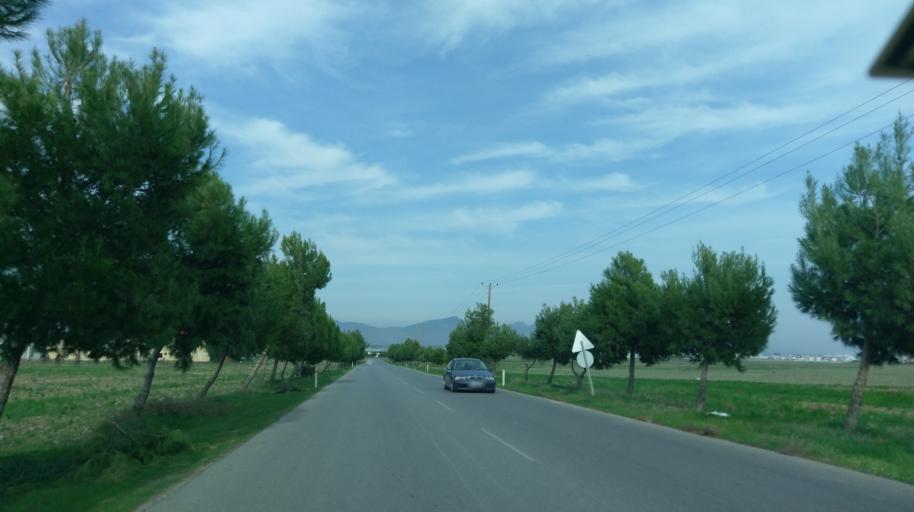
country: CY
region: Lefkosia
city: Mammari
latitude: 35.2038
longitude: 33.2725
